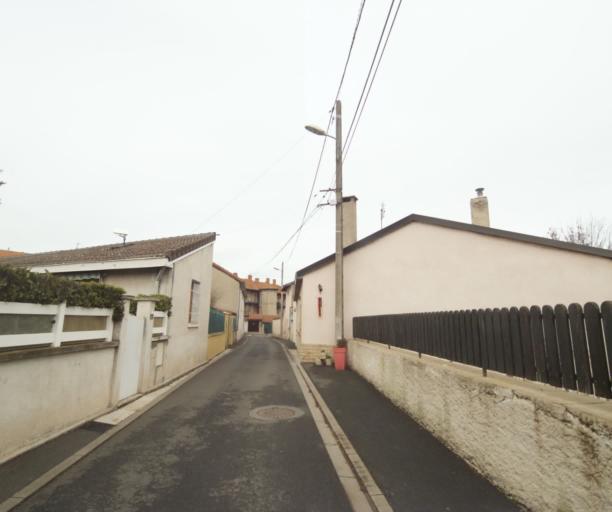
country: FR
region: Rhone-Alpes
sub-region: Departement de la Loire
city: Roanne
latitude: 46.0266
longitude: 4.0640
